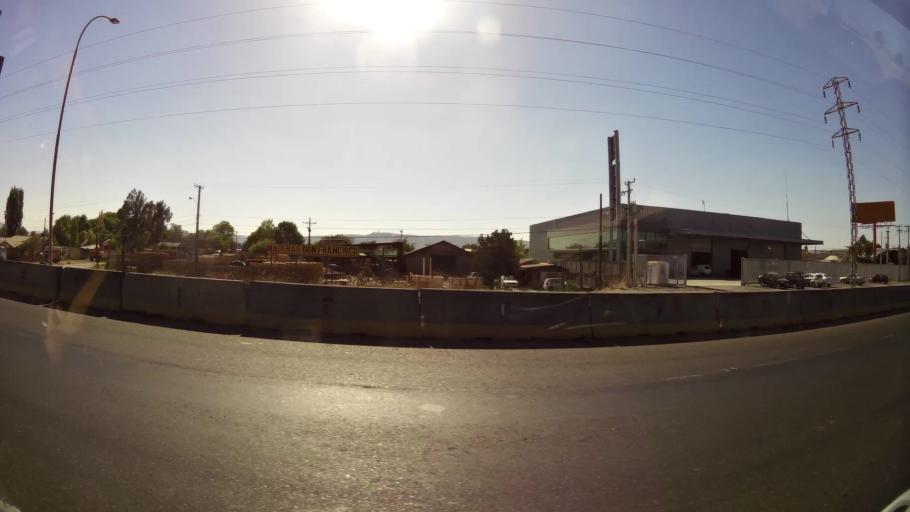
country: CL
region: Maule
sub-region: Provincia de Talca
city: Talca
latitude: -35.4258
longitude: -71.6346
